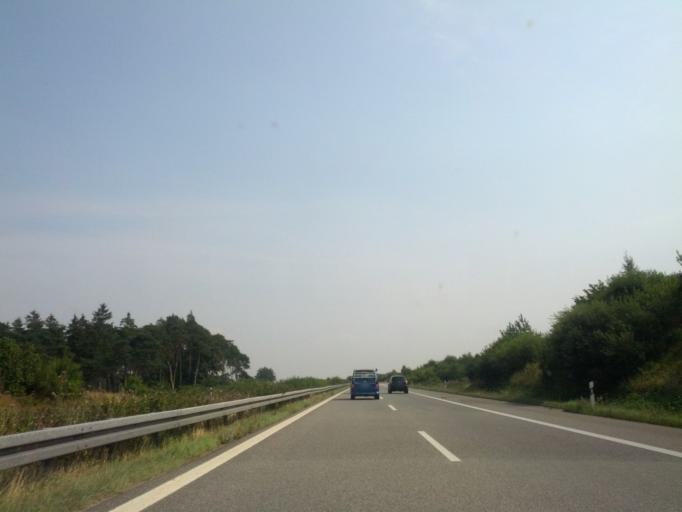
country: DE
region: Mecklenburg-Vorpommern
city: Tessin
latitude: 54.0098
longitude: 12.4988
